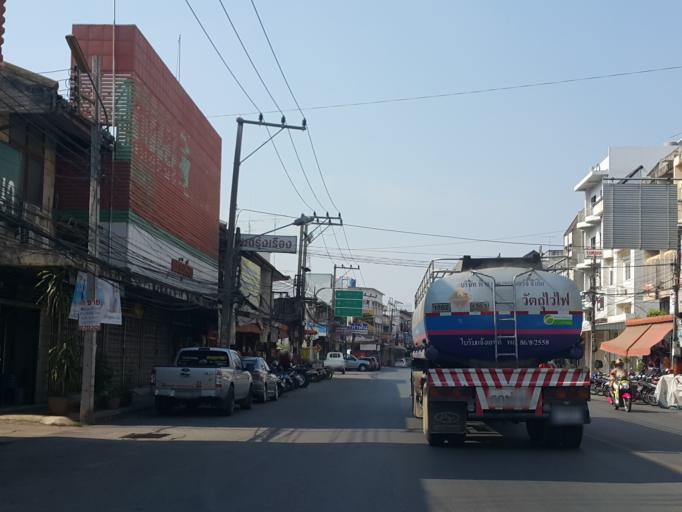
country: TH
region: Phitsanulok
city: Phitsanulok
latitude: 16.8115
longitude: 100.2642
